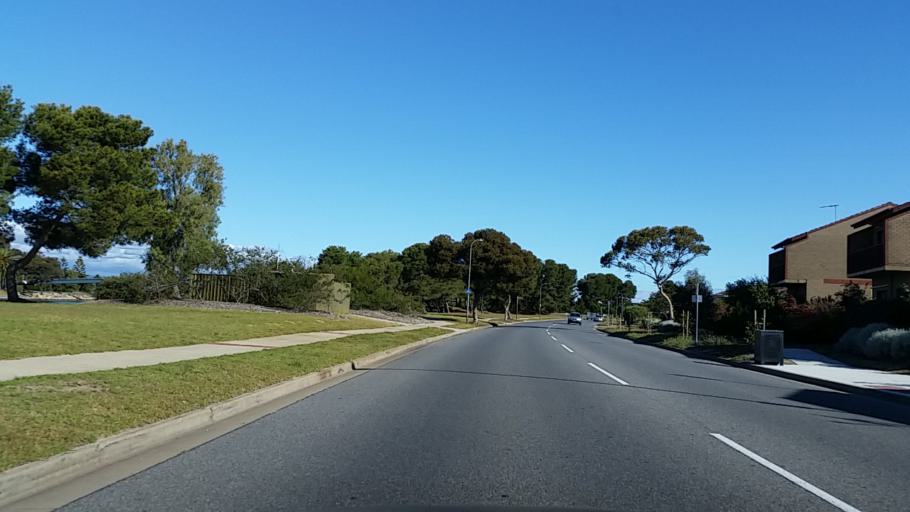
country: AU
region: South Australia
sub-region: Charles Sturt
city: West Lakes Shore
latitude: -34.8707
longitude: 138.4920
